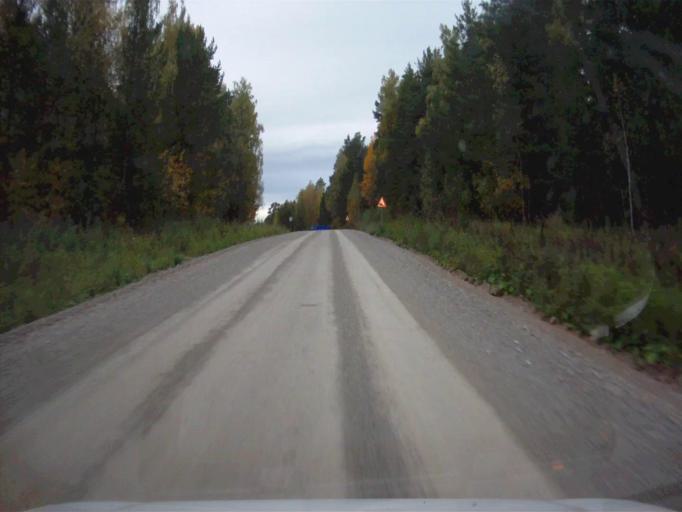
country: RU
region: Chelyabinsk
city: Nyazepetrovsk
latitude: 56.0850
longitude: 59.4196
